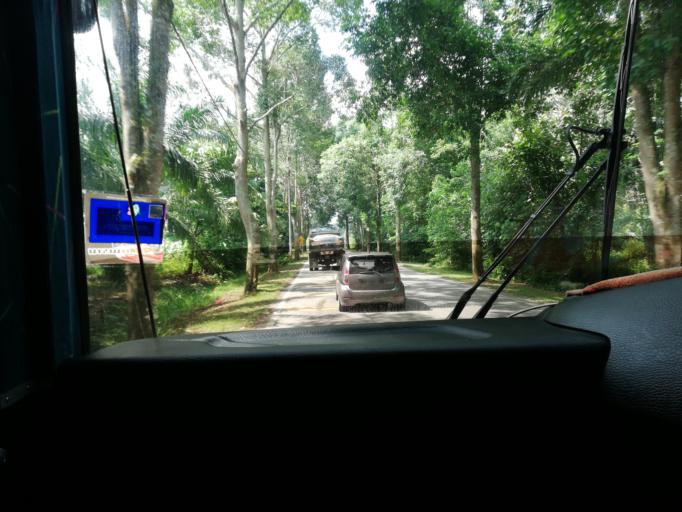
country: MY
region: Penang
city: Nibong Tebal
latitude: 5.2227
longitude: 100.6078
